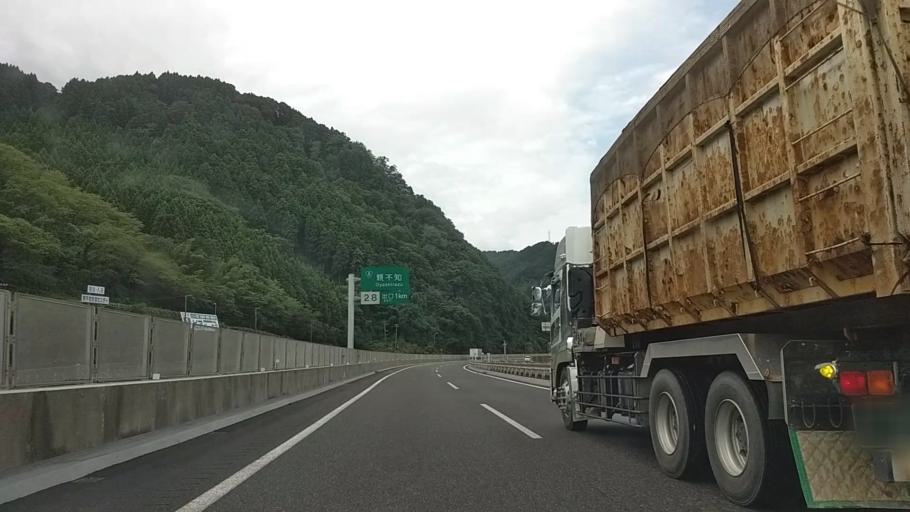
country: JP
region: Niigata
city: Itoigawa
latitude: 37.0054
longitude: 137.7353
